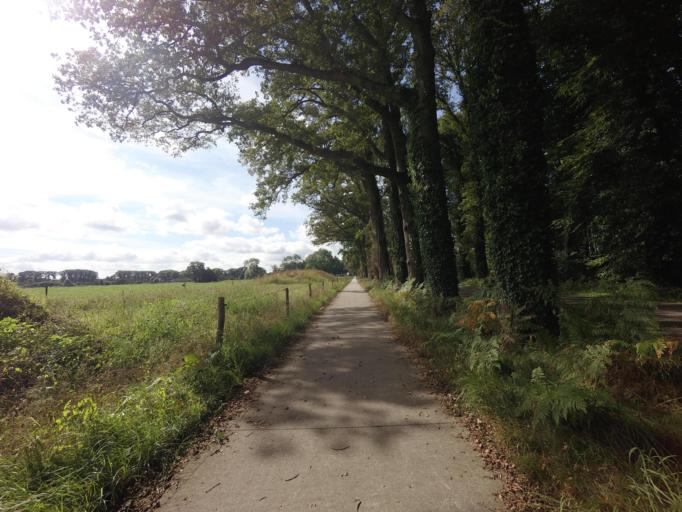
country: NL
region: Overijssel
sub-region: Gemeente Olst-Wijhe
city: Boskamp
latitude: 52.3197
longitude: 6.1717
